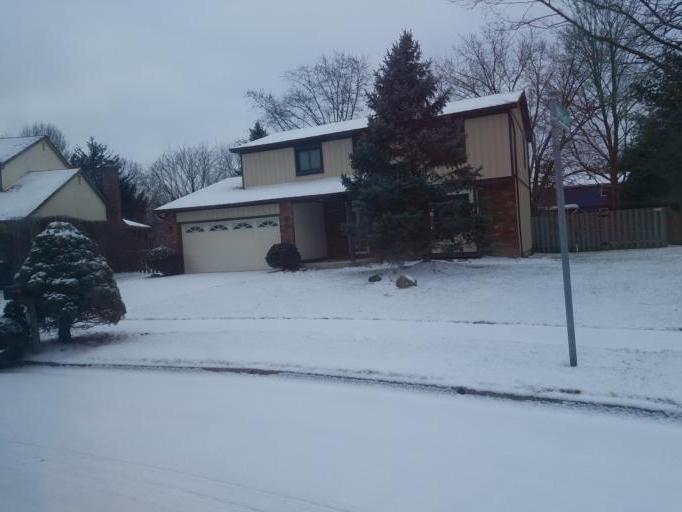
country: US
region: Ohio
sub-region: Delaware County
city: Powell
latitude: 40.1143
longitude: -83.0719
